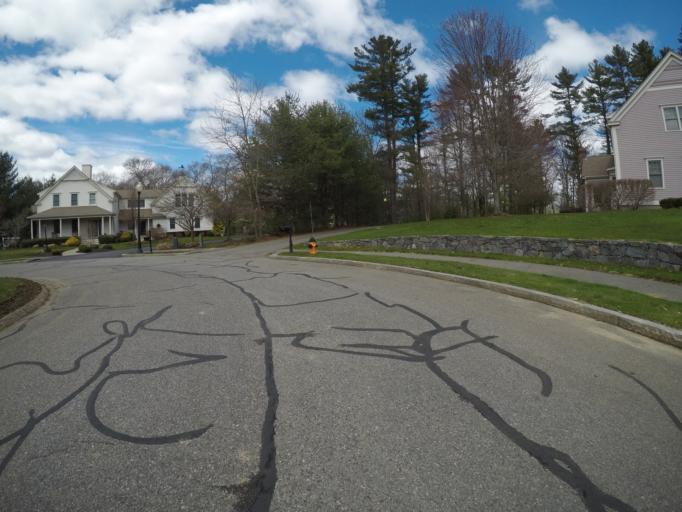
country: US
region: Massachusetts
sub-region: Norfolk County
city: Stoughton
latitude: 42.0773
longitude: -71.0910
